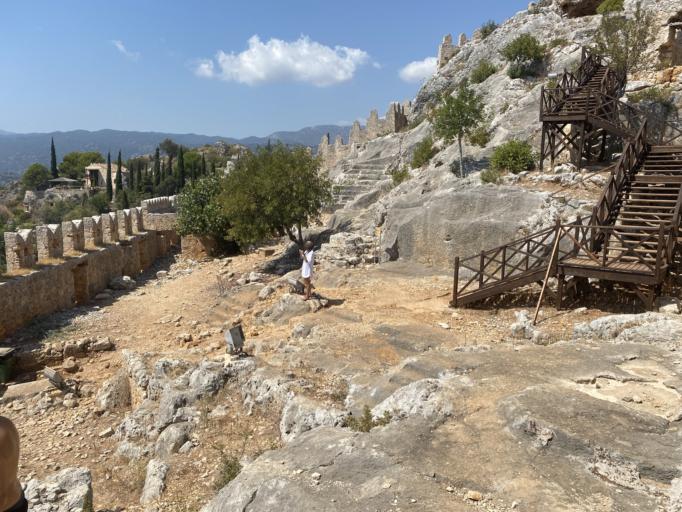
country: TR
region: Antalya
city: Demre
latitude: 36.1910
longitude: 29.8625
